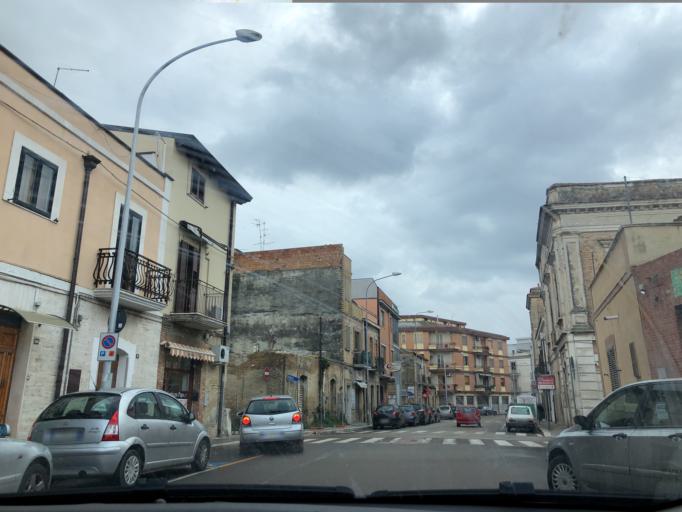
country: IT
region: Apulia
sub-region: Provincia di Foggia
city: Lucera
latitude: 41.5081
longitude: 15.3402
